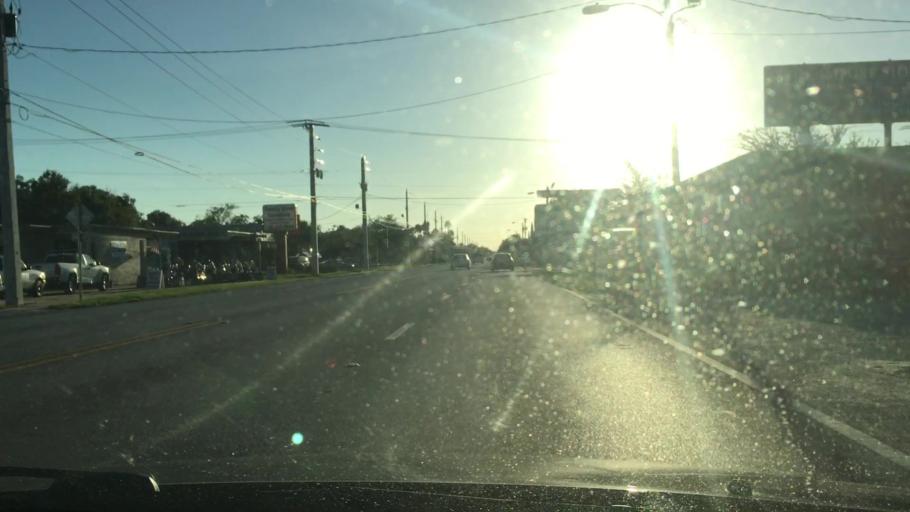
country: US
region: Florida
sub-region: Volusia County
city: Holly Hill
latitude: 29.2226
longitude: -81.0407
